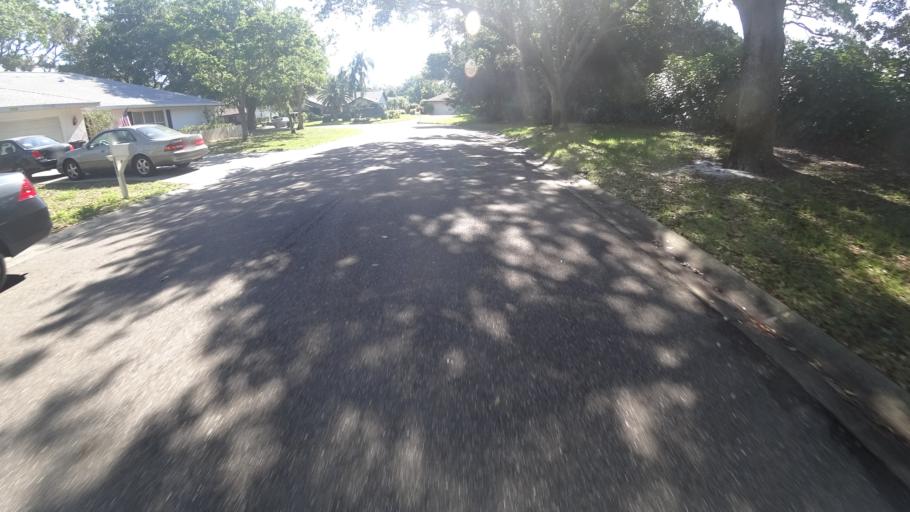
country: US
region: Florida
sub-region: Manatee County
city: West Bradenton
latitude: 27.5080
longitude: -82.6471
